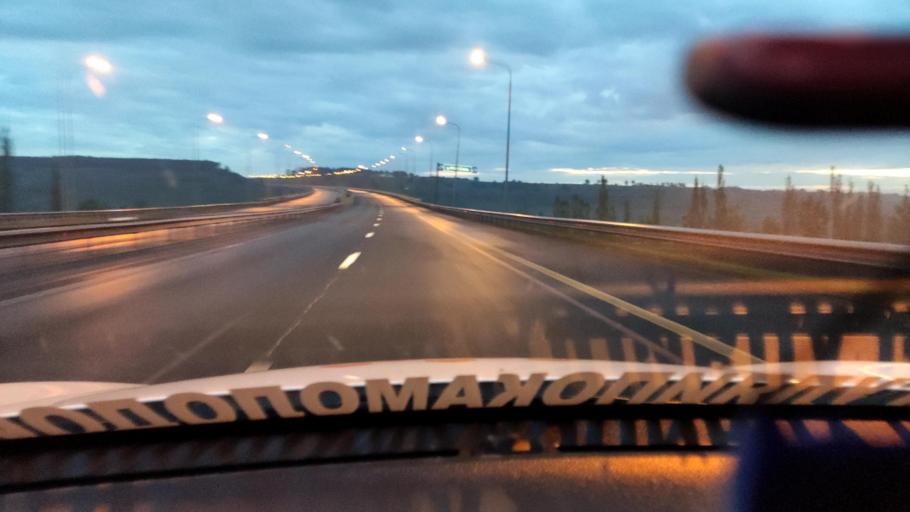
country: RU
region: Rostov
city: Tarasovskiy
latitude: 48.7257
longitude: 40.4053
